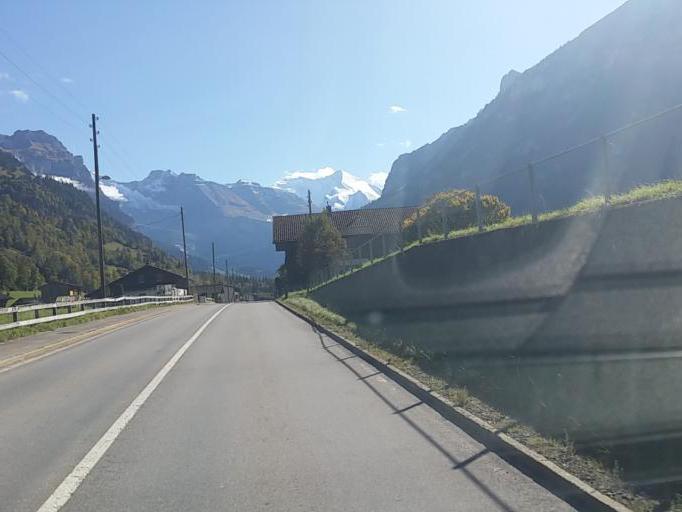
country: CH
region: Bern
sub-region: Frutigen-Niedersimmental District
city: Frutigen
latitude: 46.5644
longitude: 7.6575
